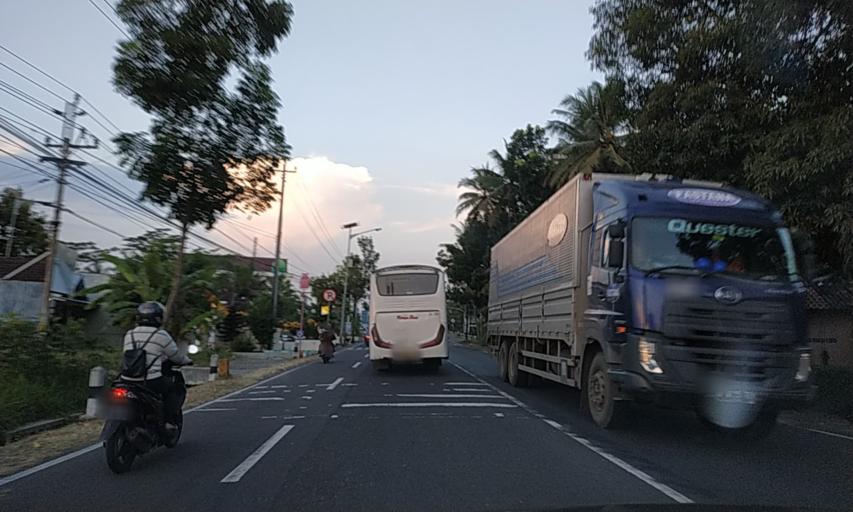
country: ID
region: Daerah Istimewa Yogyakarta
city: Srandakan
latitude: -7.8697
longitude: 110.1455
